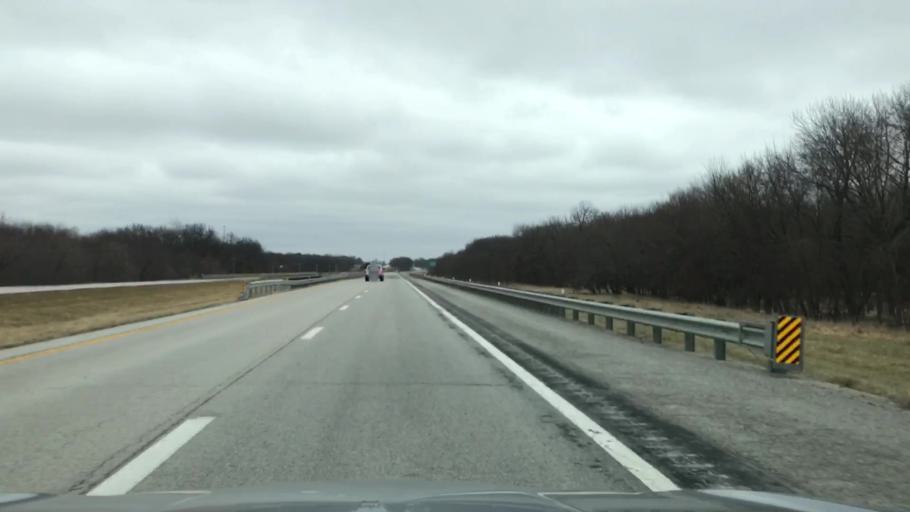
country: US
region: Missouri
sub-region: Linn County
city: Linneus
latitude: 39.7776
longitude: -93.3270
